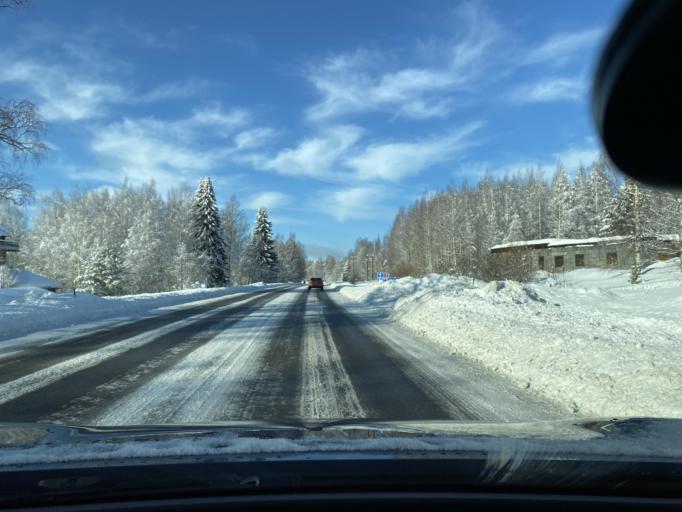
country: FI
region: Southern Savonia
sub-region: Mikkeli
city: Kangasniemi
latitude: 62.0134
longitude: 26.6240
